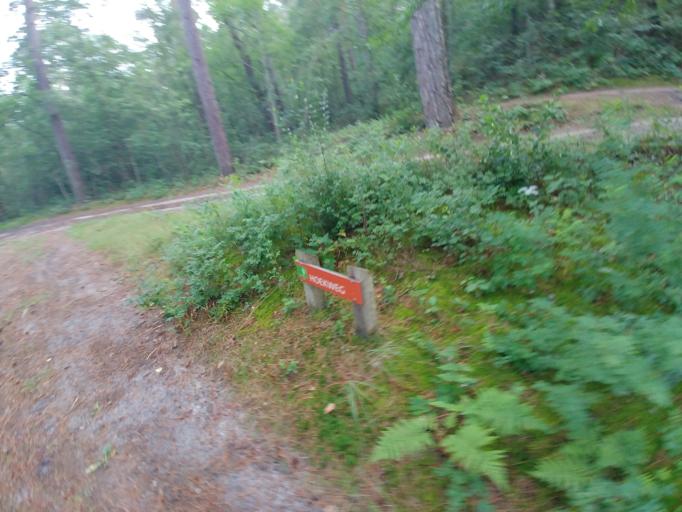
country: NL
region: North Holland
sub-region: Gemeente Bergen
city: Egmond aan Zee
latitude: 52.6864
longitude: 4.6718
